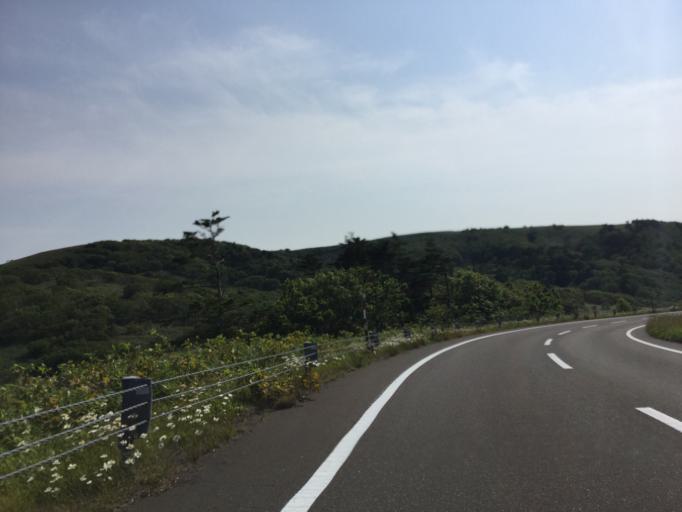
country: JP
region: Hokkaido
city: Makubetsu
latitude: 45.4967
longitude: 141.9062
